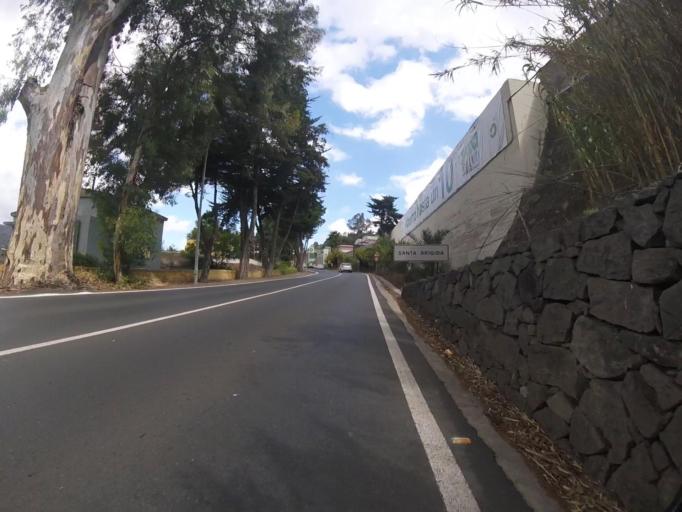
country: ES
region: Canary Islands
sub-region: Provincia de Las Palmas
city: Santa Brigida
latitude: 28.0295
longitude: -15.5001
